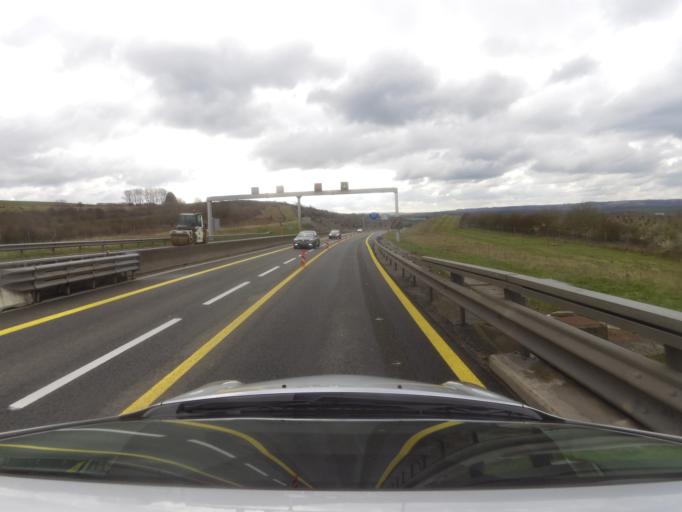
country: FR
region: Nord-Pas-de-Calais
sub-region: Departement du Pas-de-Calais
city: Isques
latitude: 50.6802
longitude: 1.6590
